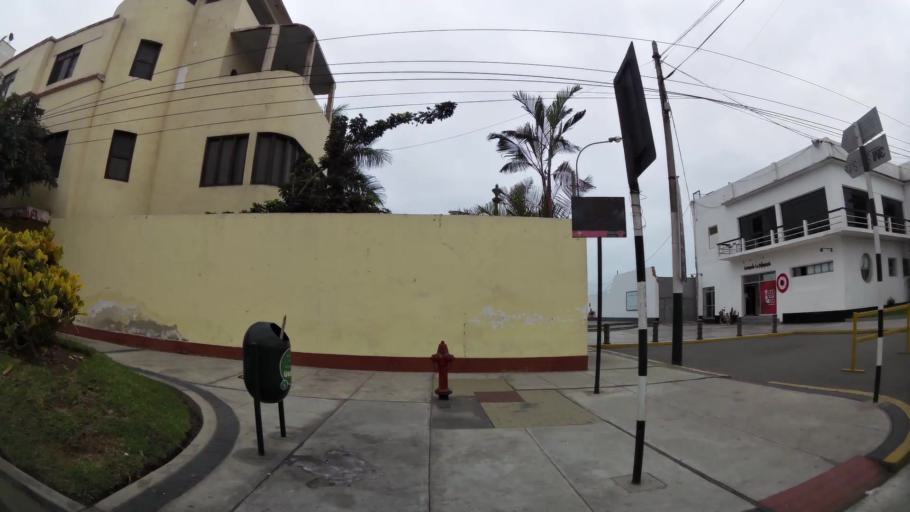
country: PE
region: Callao
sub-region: Callao
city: Callao
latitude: -12.0676
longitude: -77.1589
